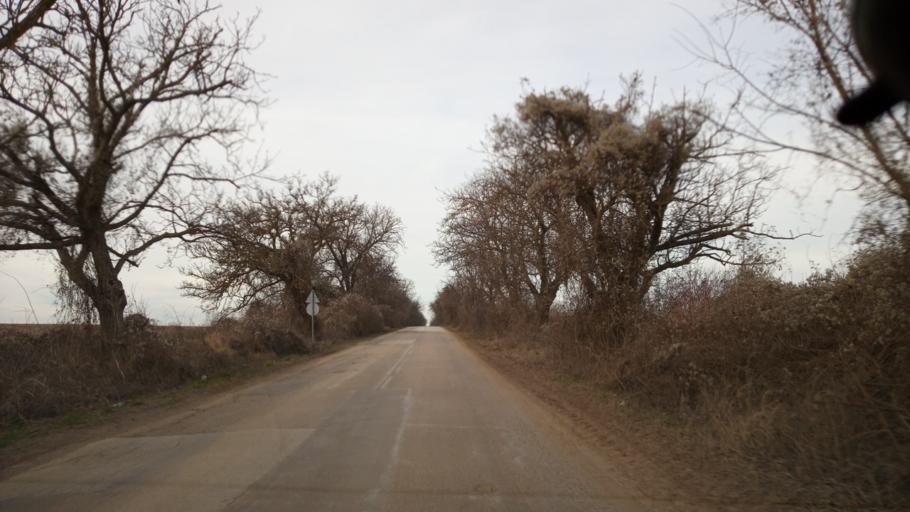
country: BG
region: Pleven
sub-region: Obshtina Nikopol
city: Nikopol
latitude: 43.5963
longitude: 24.9730
